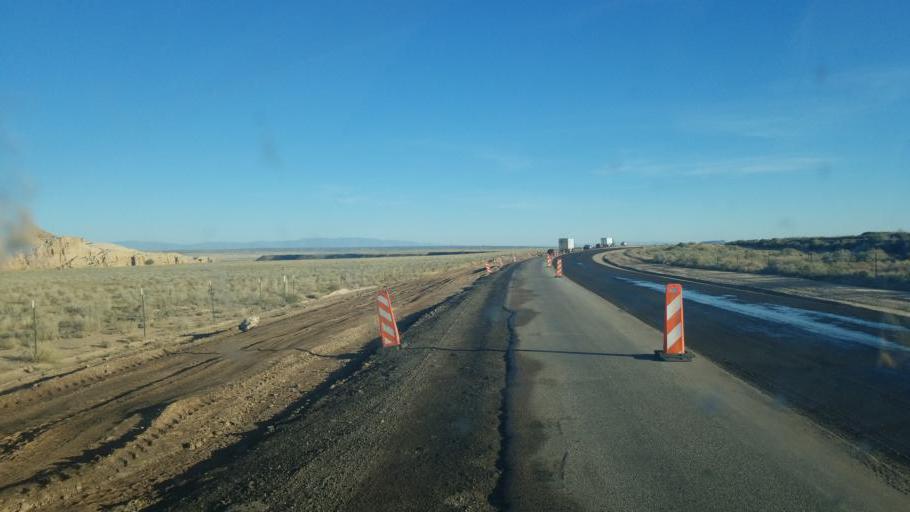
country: US
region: New Mexico
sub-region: Cibola County
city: Laguna
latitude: 34.9051
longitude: -107.0908
